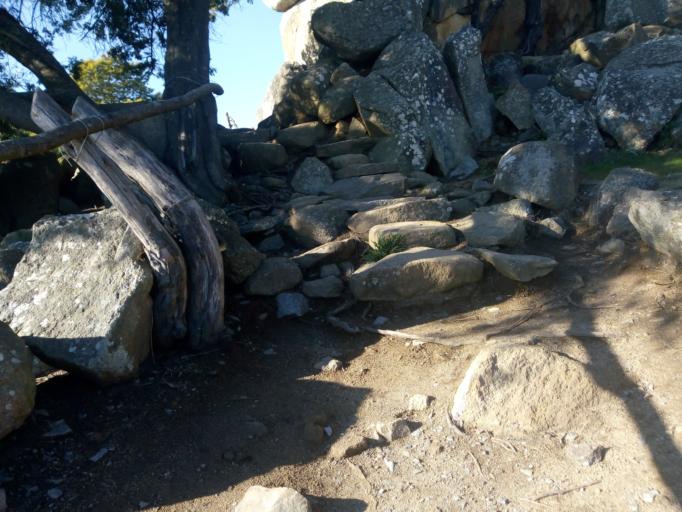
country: AR
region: Buenos Aires
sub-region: Partido de Tandil
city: Tandil
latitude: -37.3550
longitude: -59.1729
